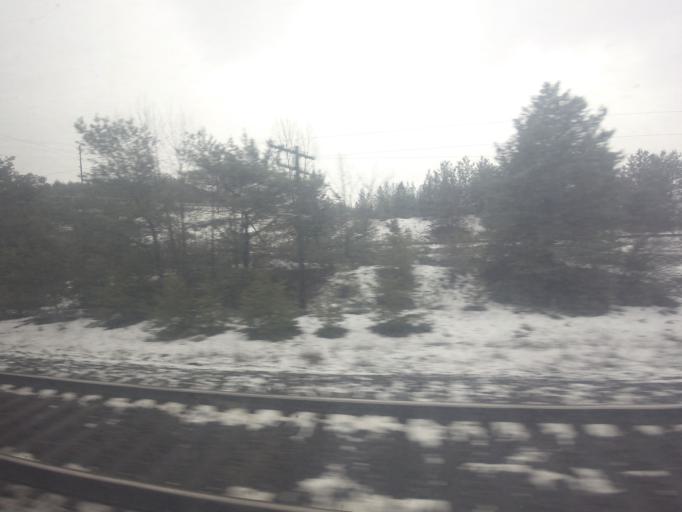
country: CA
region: Ontario
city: Quinte West
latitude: 44.0988
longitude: -77.6172
